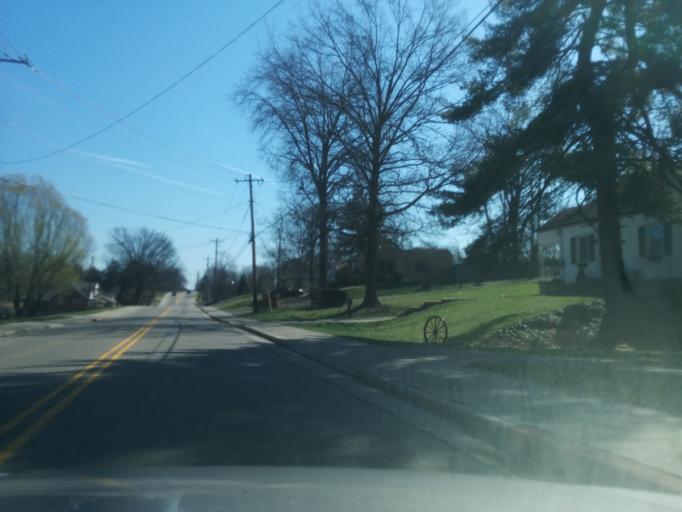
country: US
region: Ohio
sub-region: Hamilton County
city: Monfort Heights
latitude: 39.1982
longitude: -84.5919
